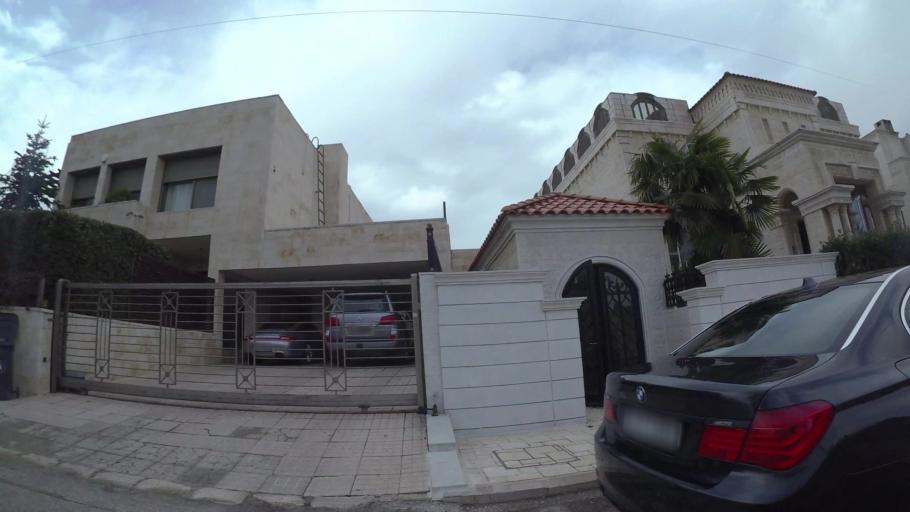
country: JO
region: Amman
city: Wadi as Sir
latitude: 31.9915
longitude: 35.8194
